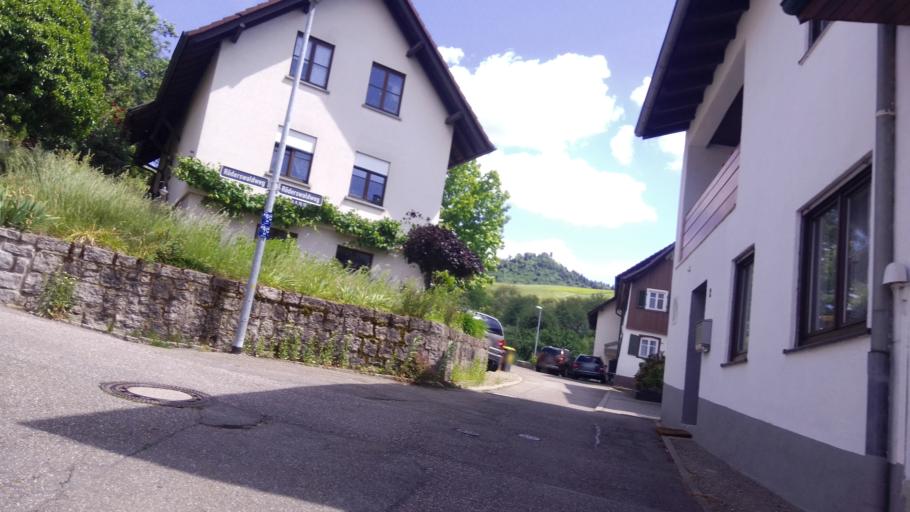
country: DE
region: Baden-Wuerttemberg
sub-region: Karlsruhe Region
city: Sinzheim
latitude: 48.7391
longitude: 8.1818
